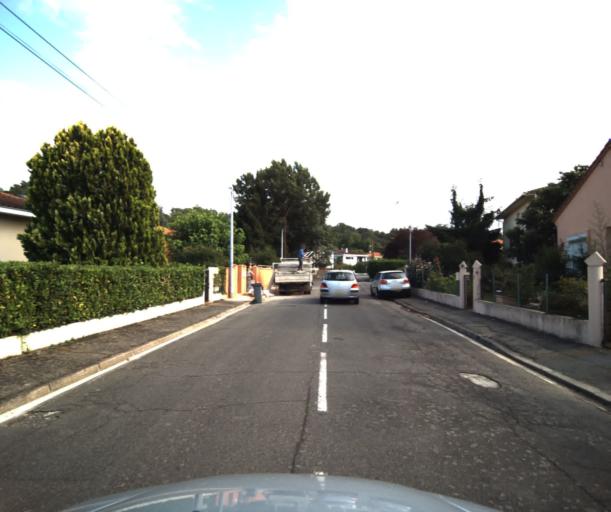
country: FR
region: Midi-Pyrenees
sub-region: Departement de la Haute-Garonne
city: Muret
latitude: 43.4554
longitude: 1.3345
